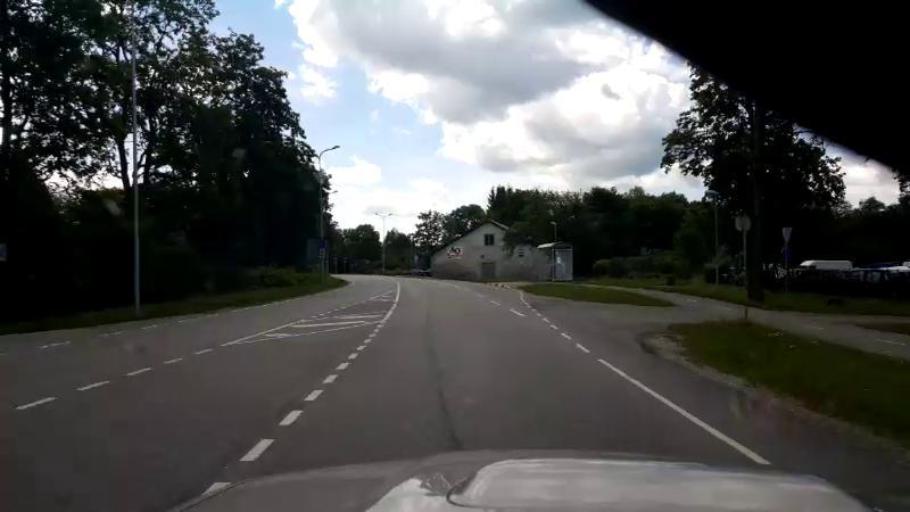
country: EE
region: Jaervamaa
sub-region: Jaerva-Jaani vald
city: Jarva-Jaani
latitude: 59.0295
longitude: 25.7026
